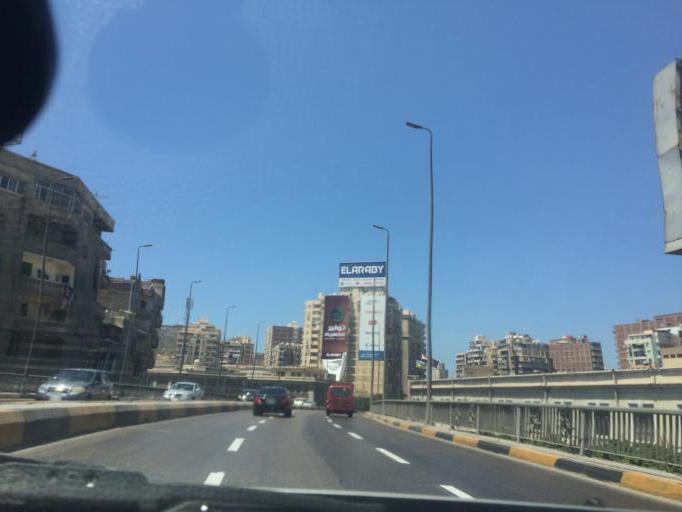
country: EG
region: Alexandria
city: Alexandria
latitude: 31.1889
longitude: 29.9239
